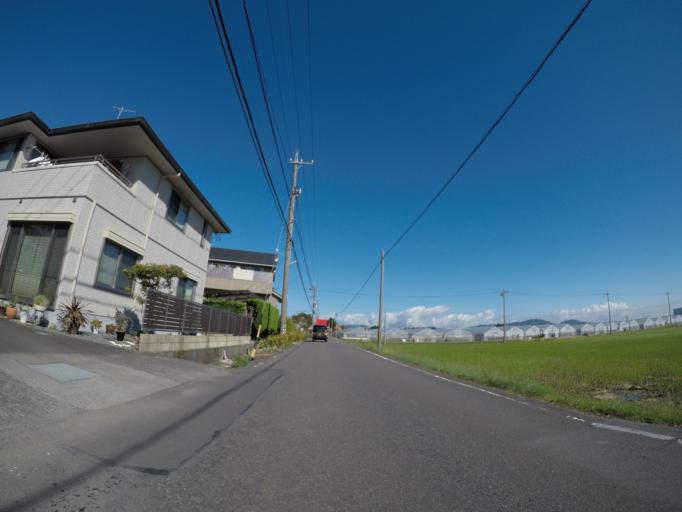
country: JP
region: Shizuoka
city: Fujieda
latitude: 34.8317
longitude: 138.2391
